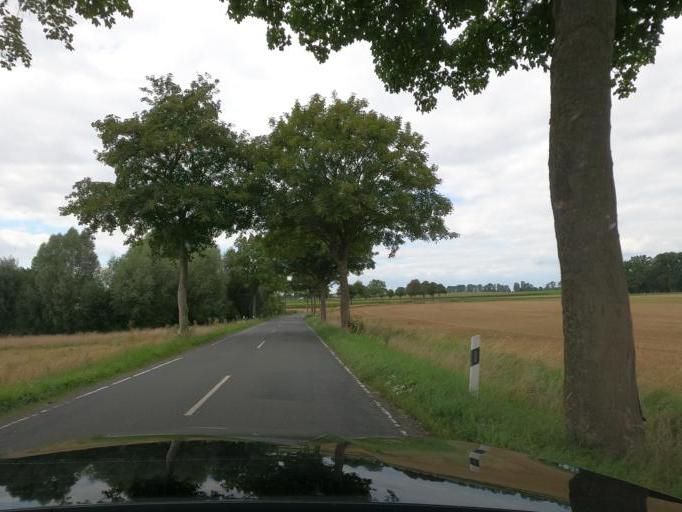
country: DE
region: Lower Saxony
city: Ilsede
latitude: 52.2185
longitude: 10.1576
